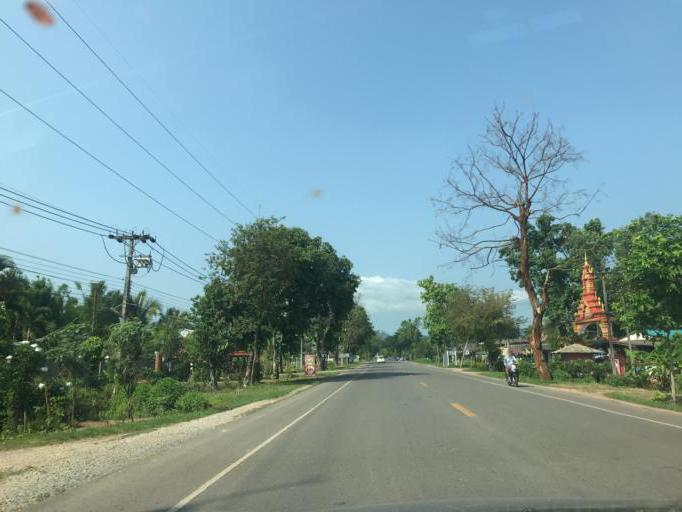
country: TH
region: Phayao
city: Chiang Kham
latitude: 19.5022
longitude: 100.2807
